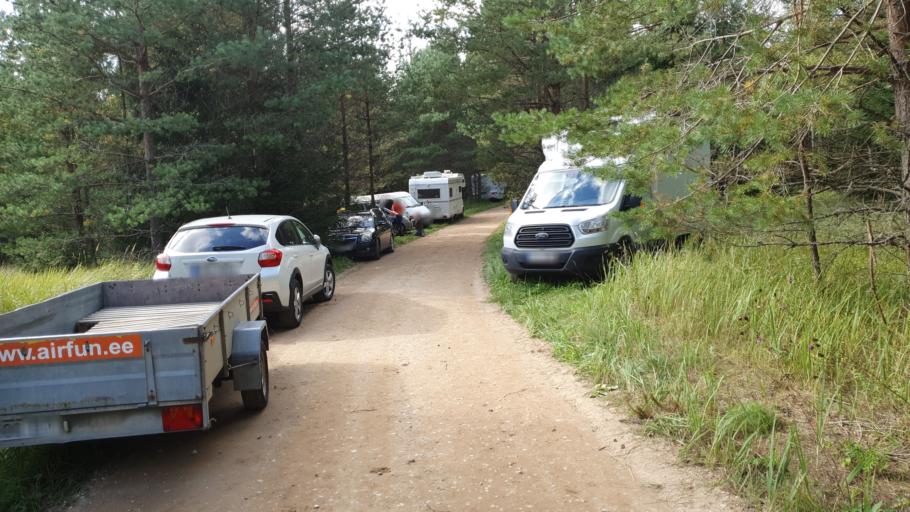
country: EE
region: Tartu
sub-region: UElenurme vald
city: Ulenurme
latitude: 58.1331
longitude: 26.7713
